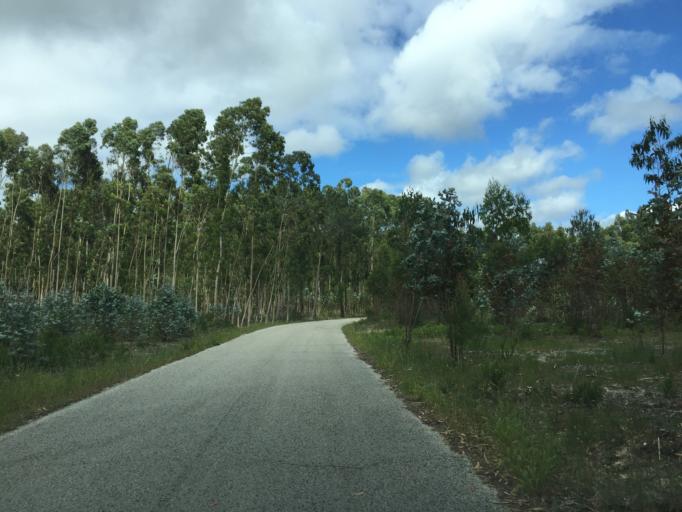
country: PT
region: Coimbra
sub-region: Figueira da Foz
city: Tavarede
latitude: 40.2109
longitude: -8.8377
